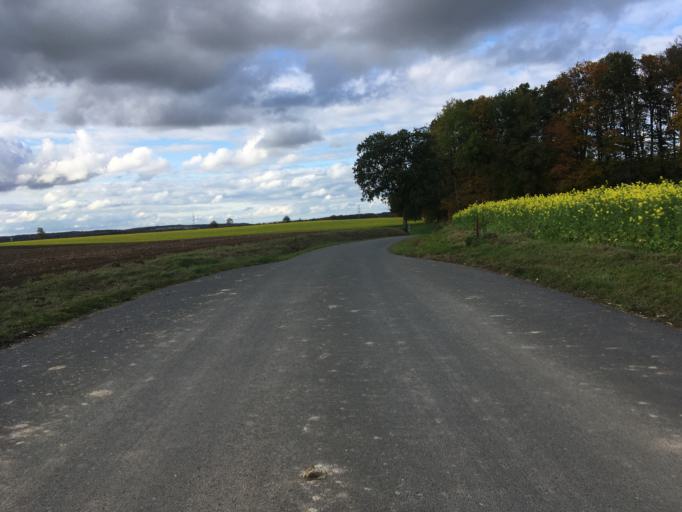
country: DE
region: Baden-Wuerttemberg
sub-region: Regierungsbezirk Stuttgart
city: Kupferzell
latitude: 49.2523
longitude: 9.7345
